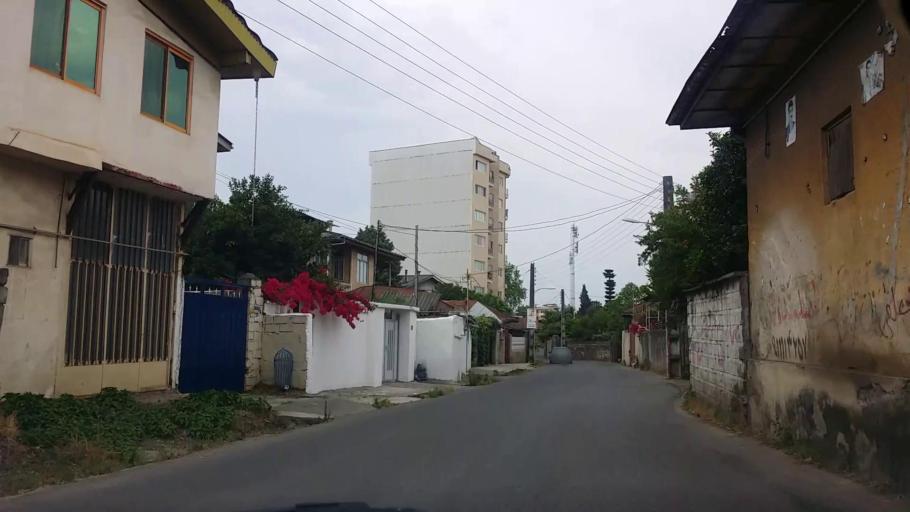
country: IR
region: Mazandaran
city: Chalus
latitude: 36.6524
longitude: 51.4164
